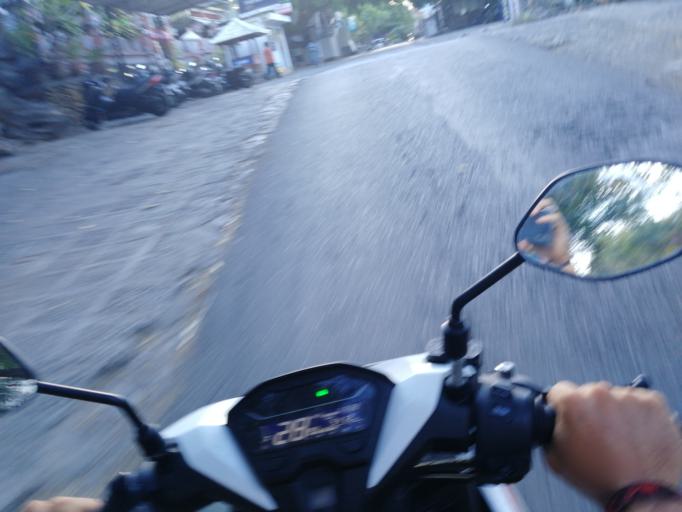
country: ID
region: Bali
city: Biaslantang Kaler
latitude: -8.3355
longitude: 115.6561
